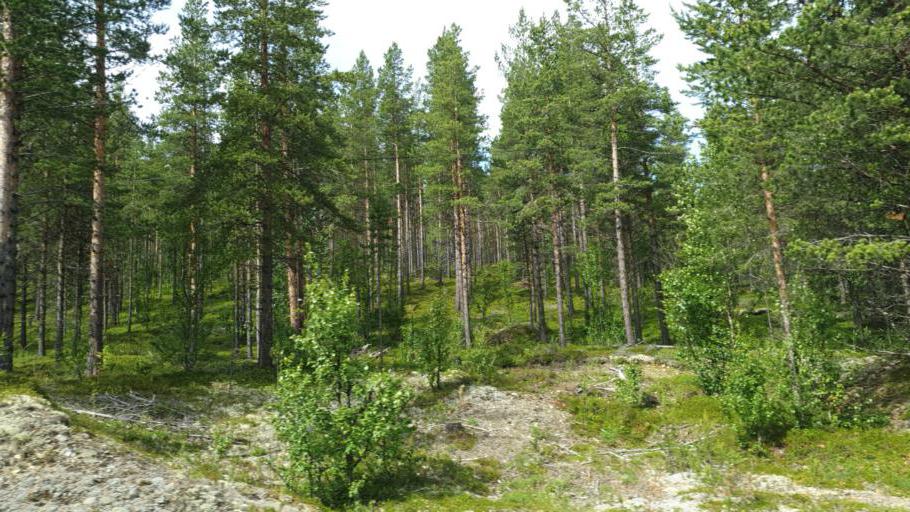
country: NO
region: Oppland
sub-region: Vaga
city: Vagamo
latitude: 61.6798
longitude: 9.0516
